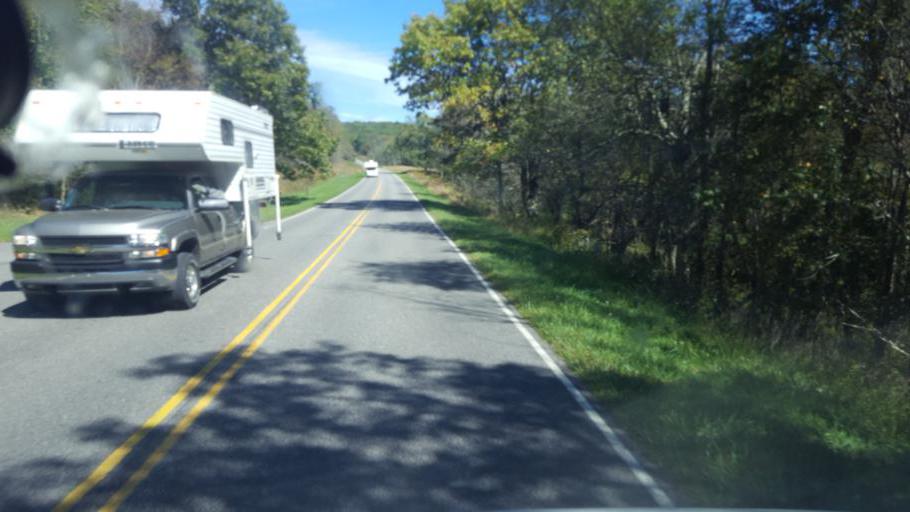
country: US
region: Virginia
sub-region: Page County
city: Stanley
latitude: 38.5004
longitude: -78.4451
